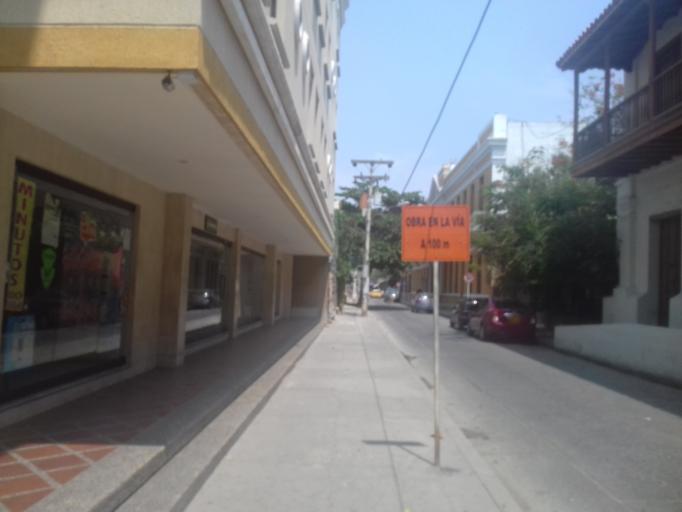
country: CO
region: Magdalena
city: Santa Marta
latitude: 11.2456
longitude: -74.2131
